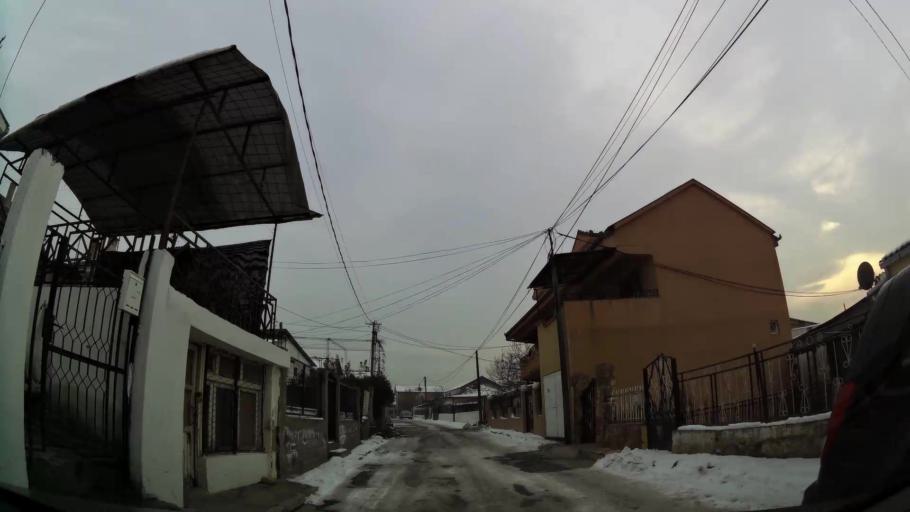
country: MK
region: Suto Orizari
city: Suto Orizare
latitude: 42.0369
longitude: 21.4275
